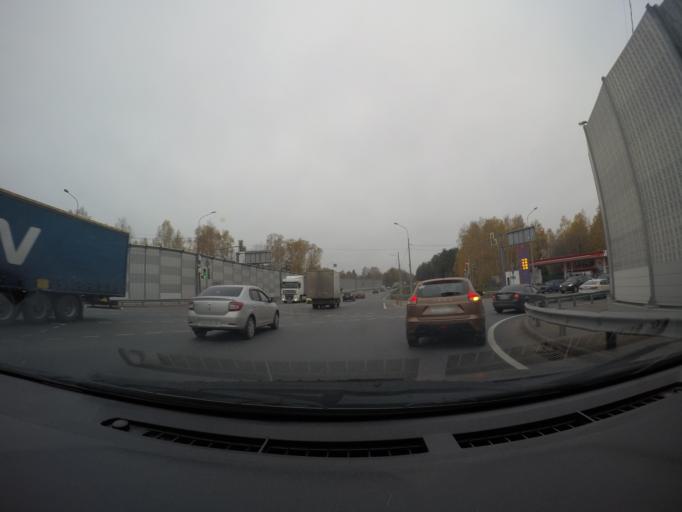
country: RU
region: Moskovskaya
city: Malyshevo
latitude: 55.4928
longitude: 38.3729
